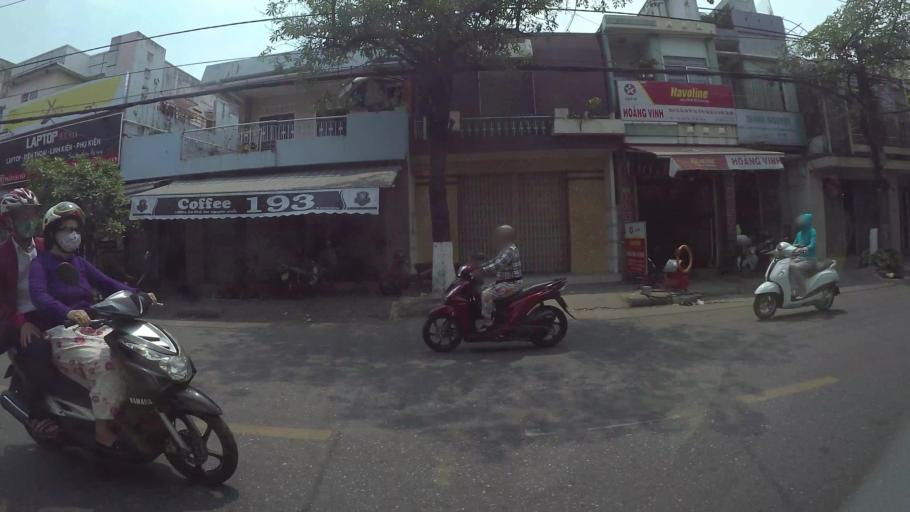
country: VN
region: Da Nang
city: Thanh Khe
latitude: 16.0714
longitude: 108.2017
